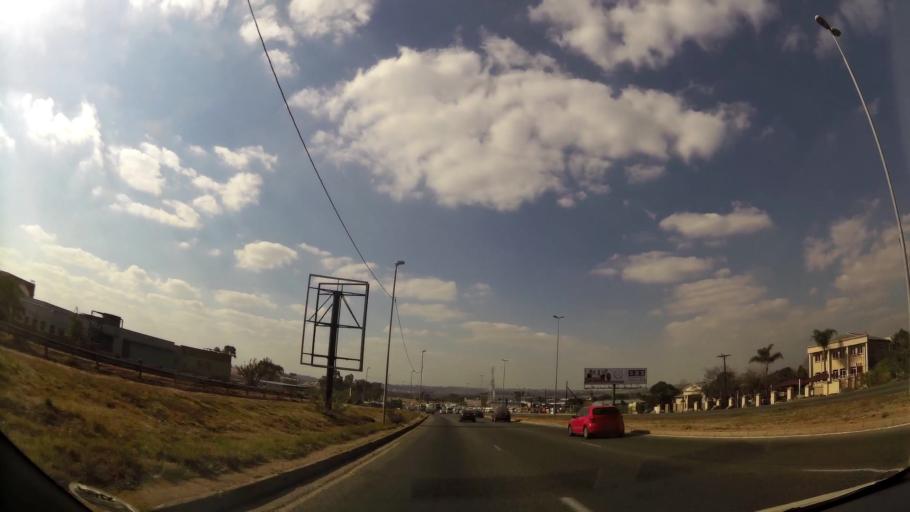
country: ZA
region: Gauteng
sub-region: West Rand District Municipality
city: Muldersdriseloop
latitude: -26.0634
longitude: 27.8305
